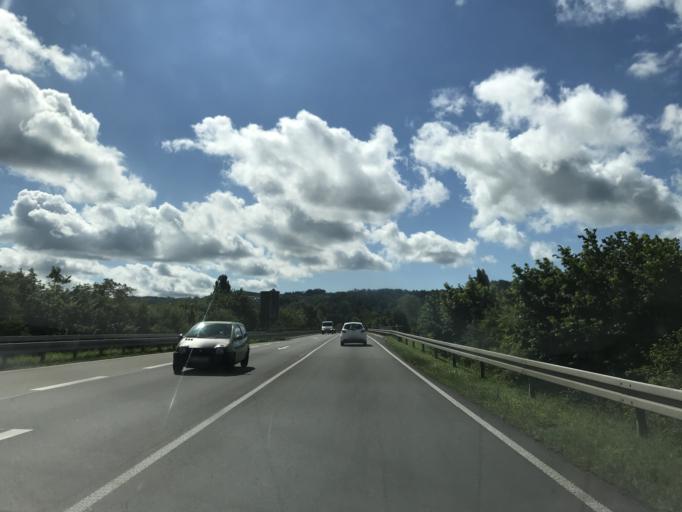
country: DE
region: Baden-Wuerttemberg
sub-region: Freiburg Region
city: Maulburg
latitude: 47.6458
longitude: 7.7950
